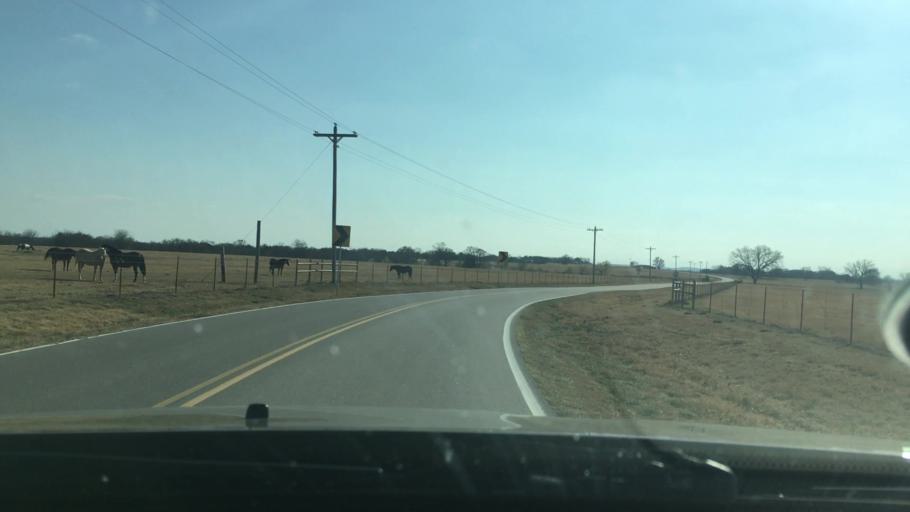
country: US
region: Oklahoma
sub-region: Marshall County
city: Oakland
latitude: 34.0244
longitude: -96.9309
